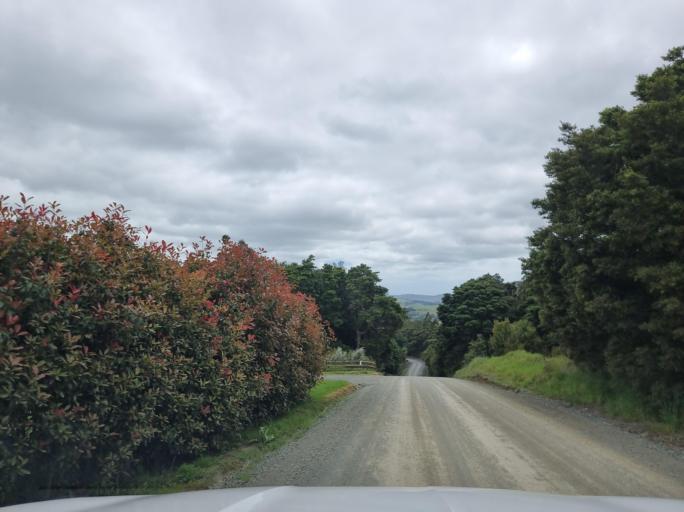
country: NZ
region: Auckland
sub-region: Auckland
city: Wellsford
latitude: -36.1638
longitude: 174.5521
